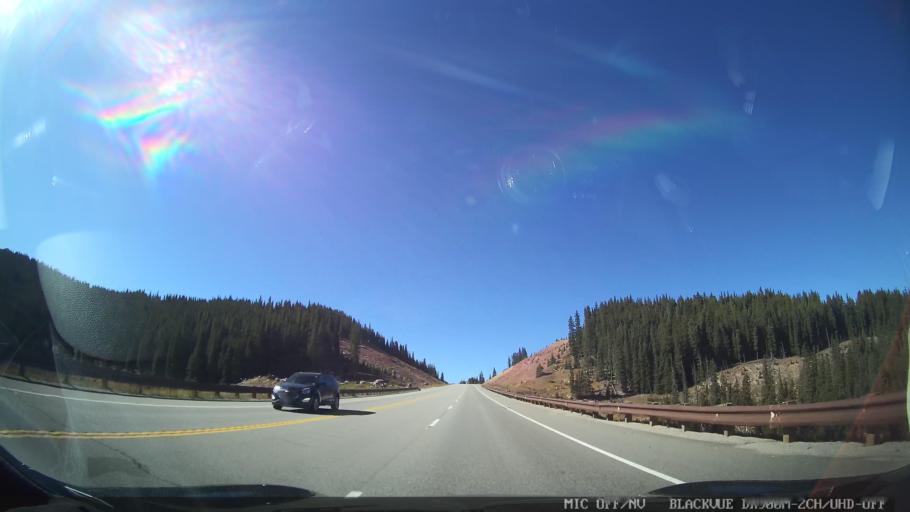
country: US
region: Colorado
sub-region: Summit County
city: Breckenridge
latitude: 39.4147
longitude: -106.1741
